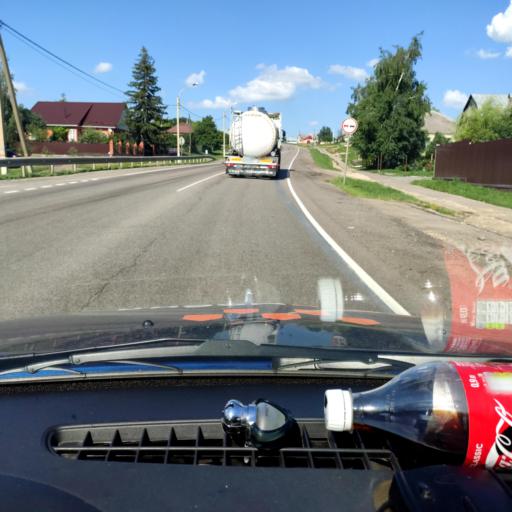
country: RU
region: Lipetsk
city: Kazaki
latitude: 52.6291
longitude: 38.2749
